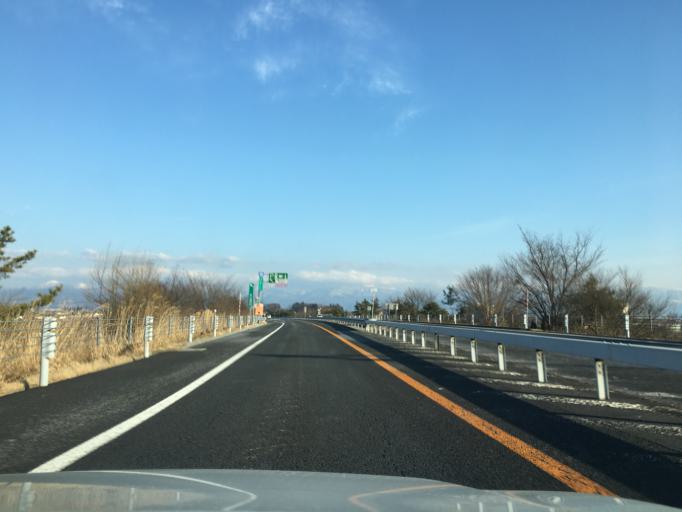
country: JP
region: Yamagata
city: Sagae
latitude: 38.3688
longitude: 140.2519
